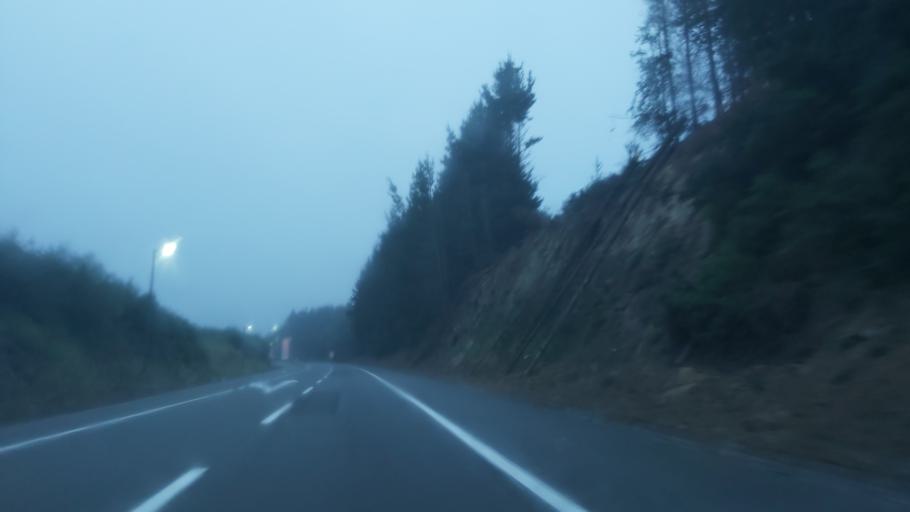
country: CL
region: Biobio
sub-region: Provincia de Concepcion
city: Penco
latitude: -36.7452
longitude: -72.9165
